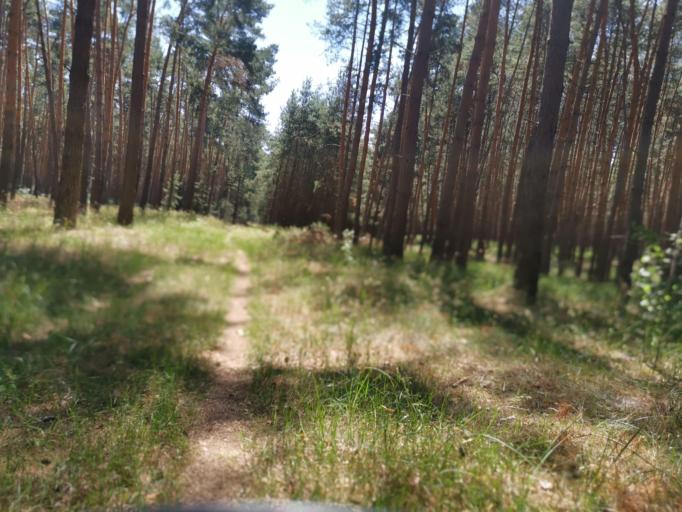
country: CZ
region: South Moravian
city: Bzenec
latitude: 48.9248
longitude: 17.2452
